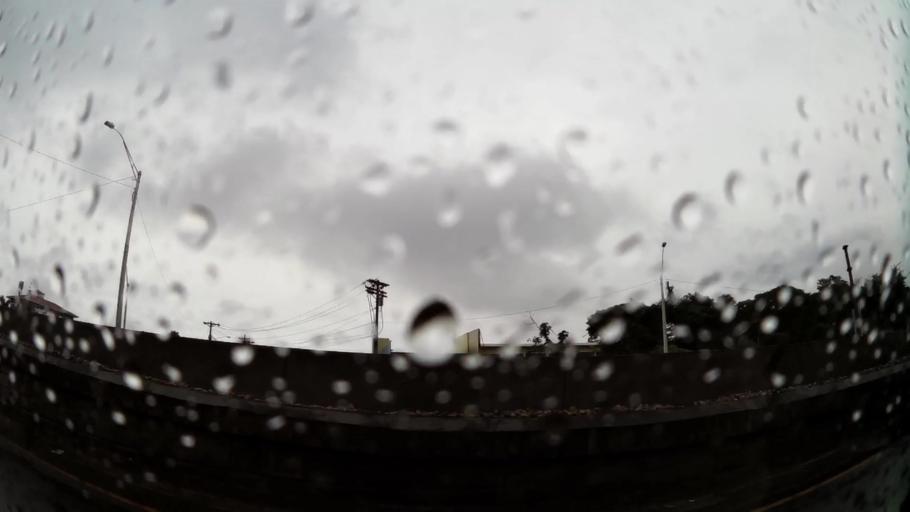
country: PA
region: Colon
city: Arco Iris
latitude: 9.3367
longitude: -79.8870
